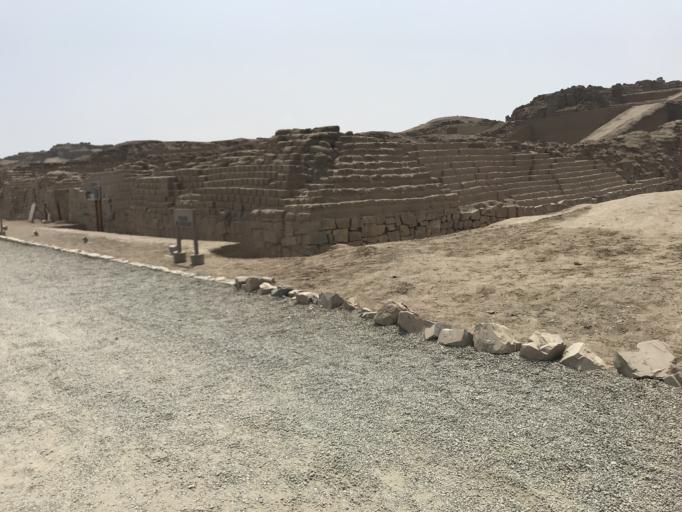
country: PE
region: Lima
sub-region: Lima
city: Punta Hermosa
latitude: -12.2567
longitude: -76.9024
